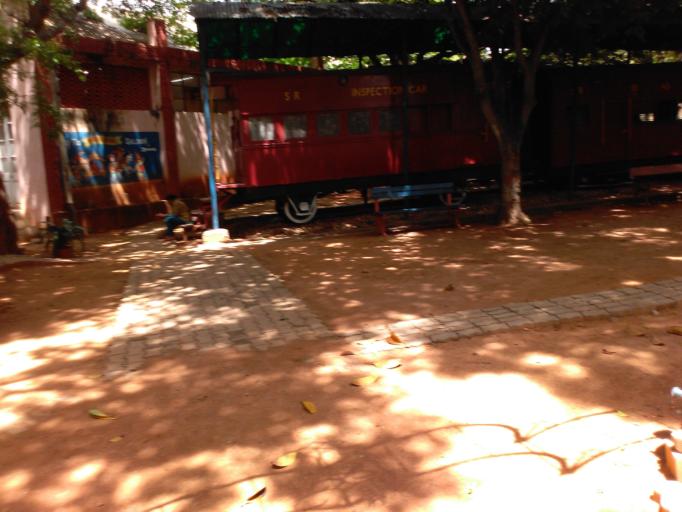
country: IN
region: Karnataka
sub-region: Mysore
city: Mysore
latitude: 12.3138
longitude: 76.6451
